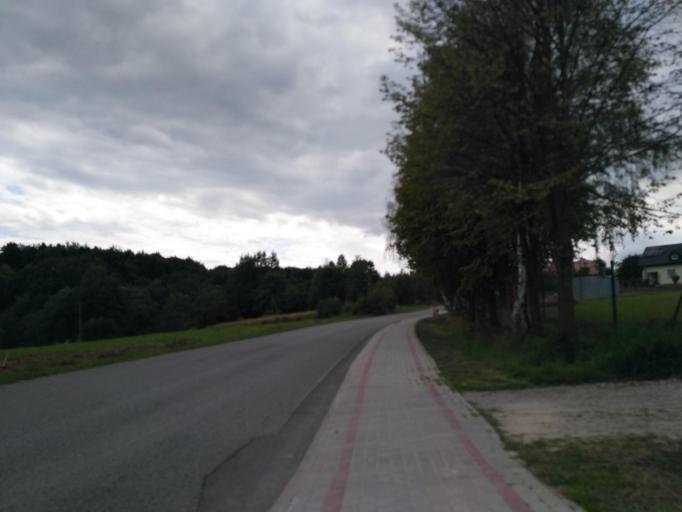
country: PL
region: Subcarpathian Voivodeship
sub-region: Powiat rzeszowski
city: Straszydle
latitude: 49.8911
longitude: 21.9975
